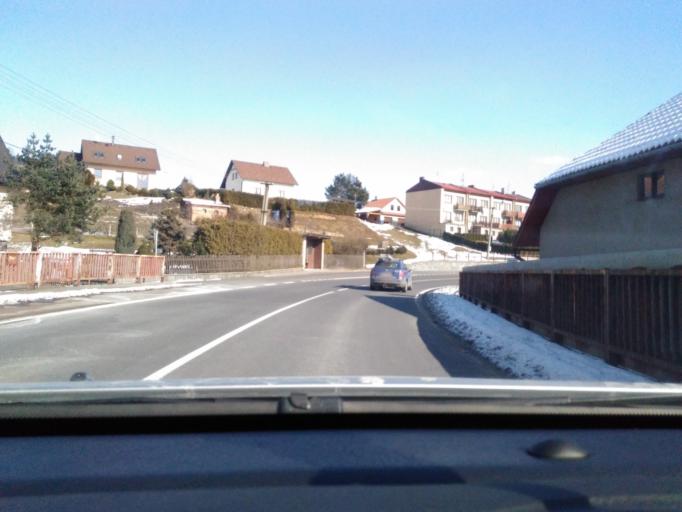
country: CZ
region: Vysocina
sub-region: Okres Zd'ar nad Sazavou
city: Nove Mesto na Morave
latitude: 49.5482
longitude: 16.1581
